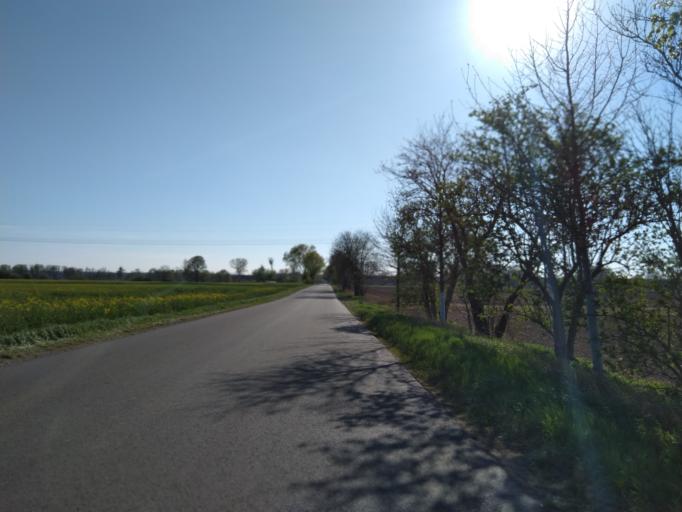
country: DE
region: Brandenburg
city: Bliesdorf
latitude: 52.6984
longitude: 14.1766
